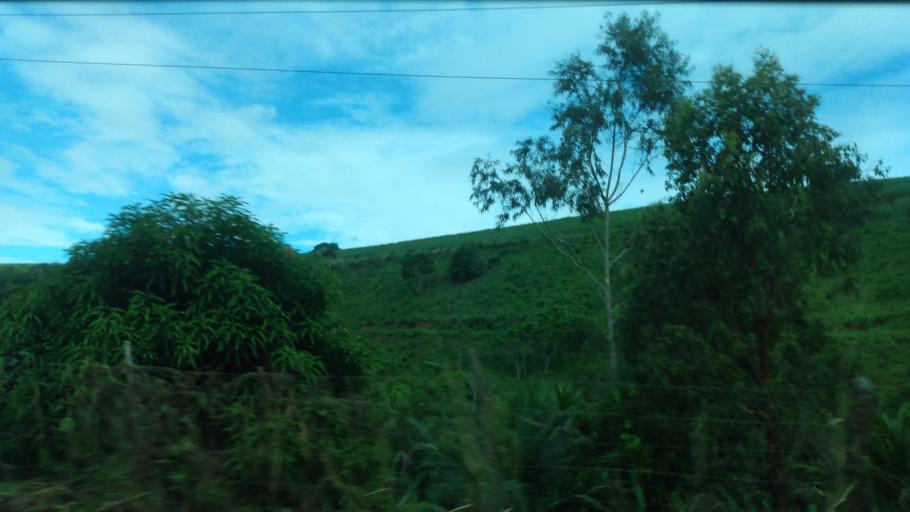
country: BR
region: Pernambuco
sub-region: Catende
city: Catende
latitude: -8.7106
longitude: -35.7677
